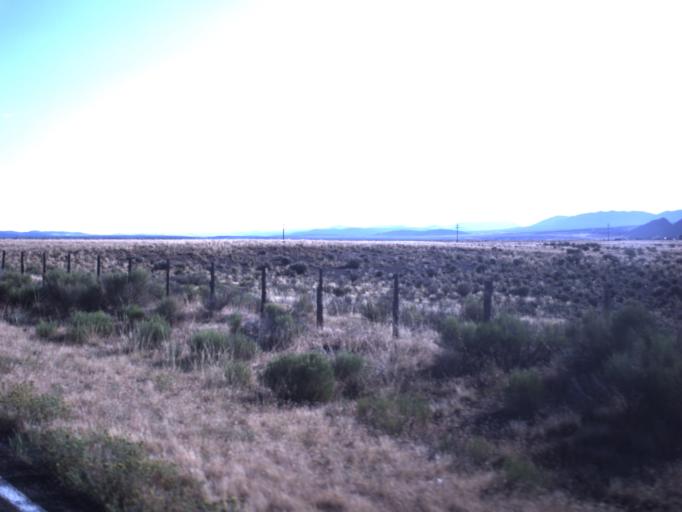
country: US
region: Utah
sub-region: Iron County
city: Enoch
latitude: 37.8870
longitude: -113.0316
